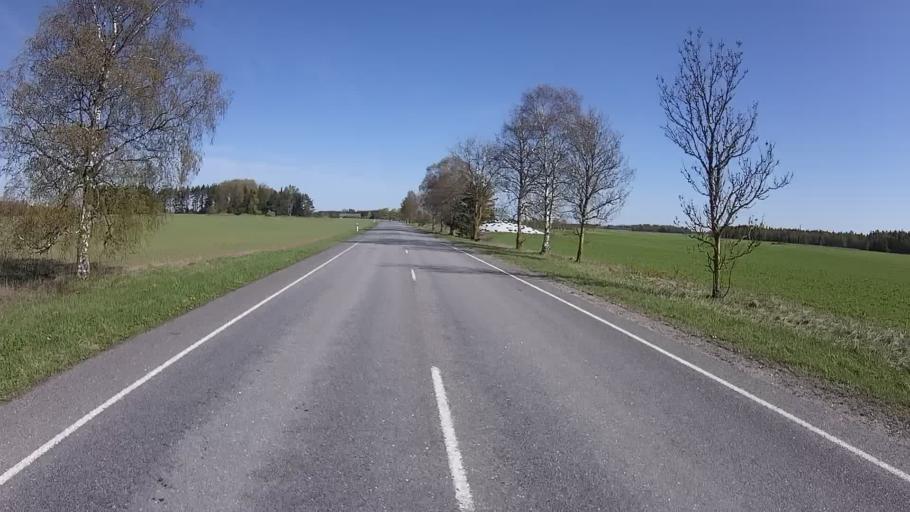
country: EE
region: Raplamaa
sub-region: Kehtna vald
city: Kehtna
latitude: 58.8921
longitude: 24.7885
